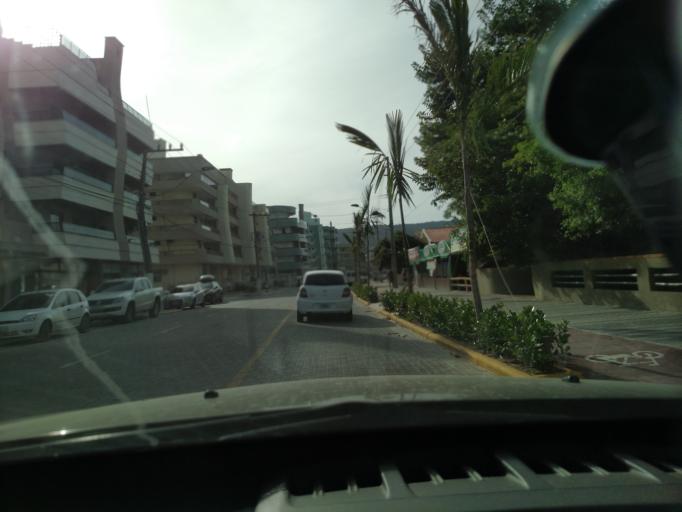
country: BR
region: Santa Catarina
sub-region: Porto Belo
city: Porto Belo
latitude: -27.1469
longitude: -48.5009
